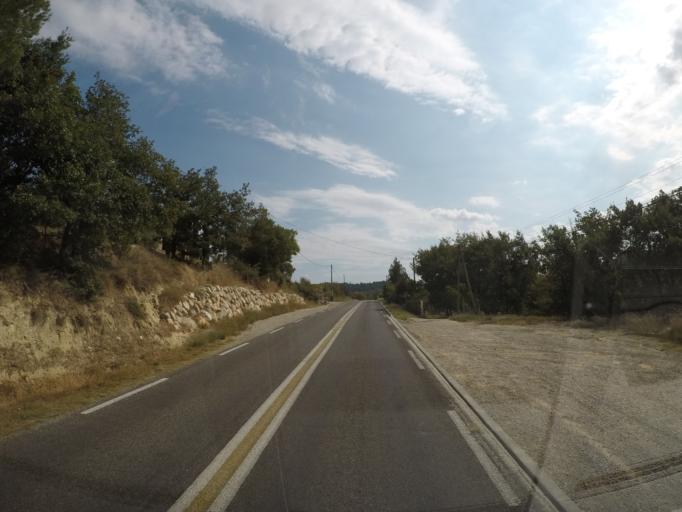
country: FR
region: Provence-Alpes-Cote d'Azur
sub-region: Departement du Vaucluse
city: Ansouis
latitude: 43.7364
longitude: 5.4783
